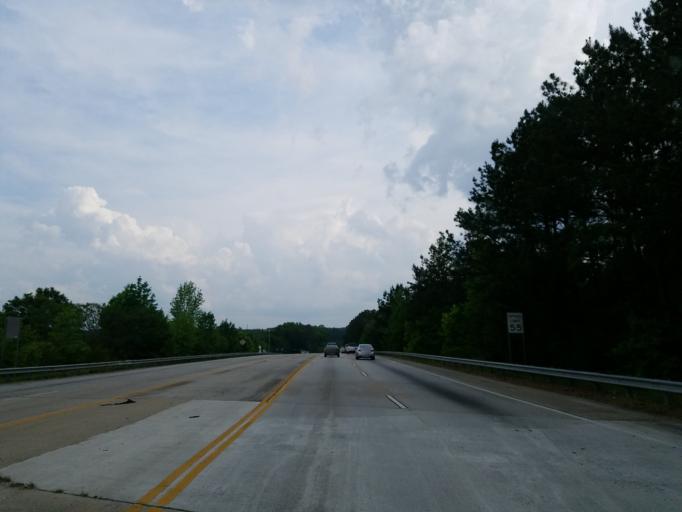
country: US
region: Georgia
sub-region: Cobb County
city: Powder Springs
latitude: 33.8649
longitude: -84.6970
